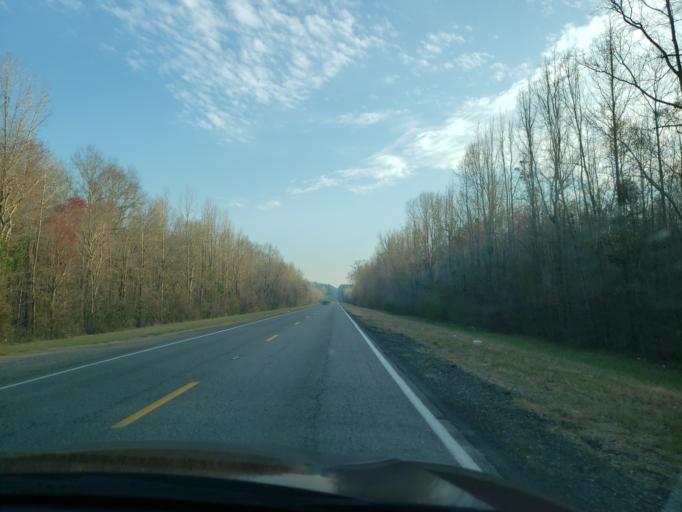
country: US
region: Alabama
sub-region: Hale County
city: Greensboro
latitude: 32.7694
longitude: -87.5855
